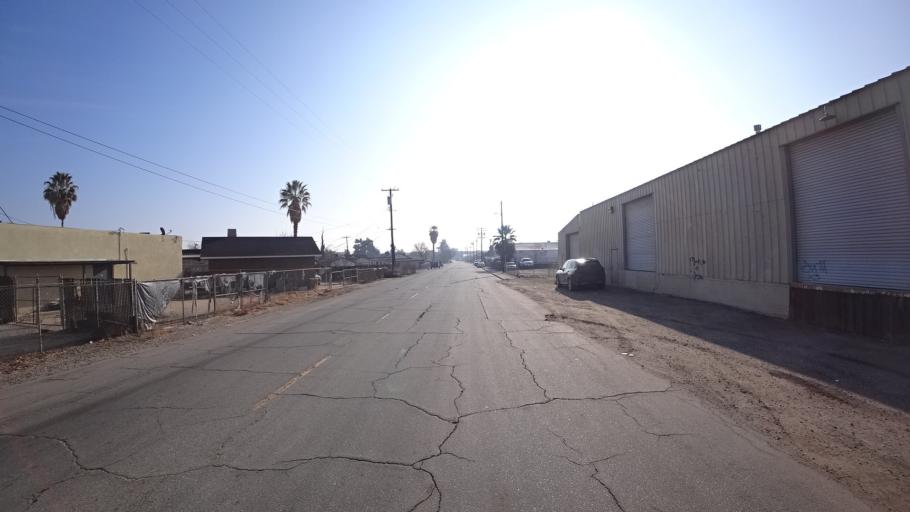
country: US
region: California
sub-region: Kern County
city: Bakersfield
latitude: 35.3862
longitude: -119.0136
